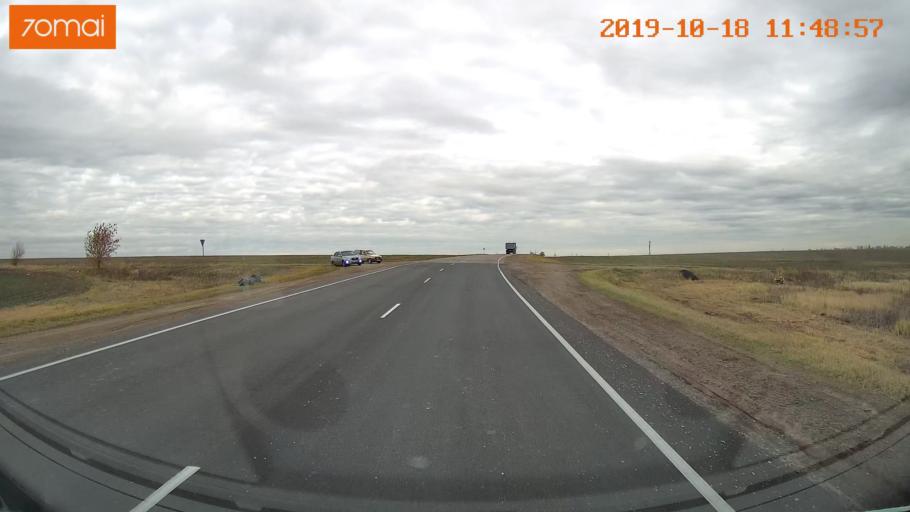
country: RU
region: Rjazan
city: Mikhaylov
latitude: 54.2443
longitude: 38.9855
